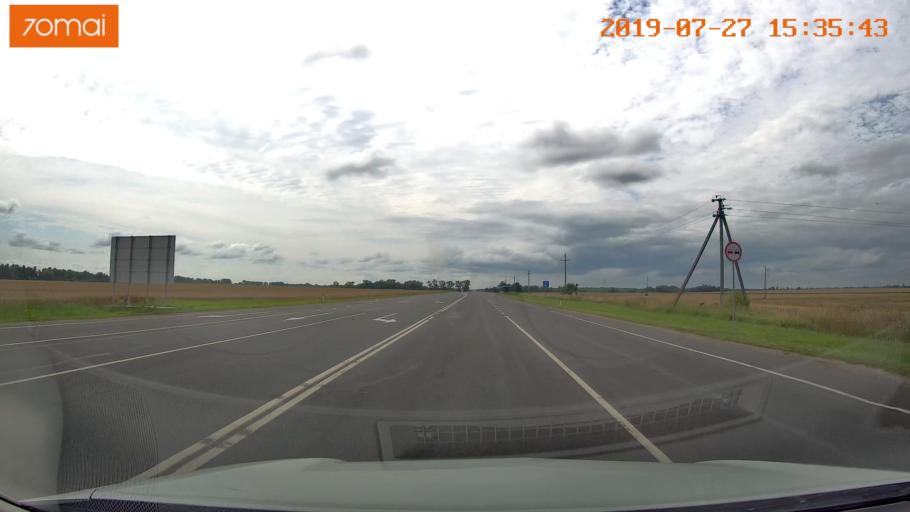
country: RU
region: Kaliningrad
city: Nesterov
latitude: 54.6132
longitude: 22.3895
